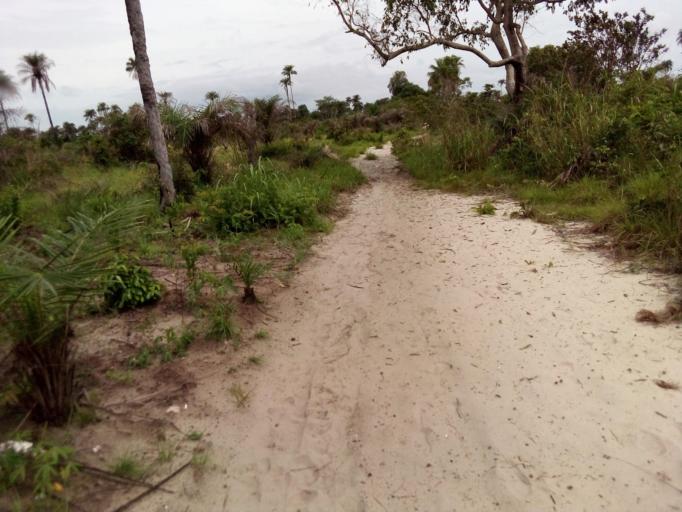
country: SL
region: Southern Province
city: Bonthe
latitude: 7.5203
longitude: -12.5741
